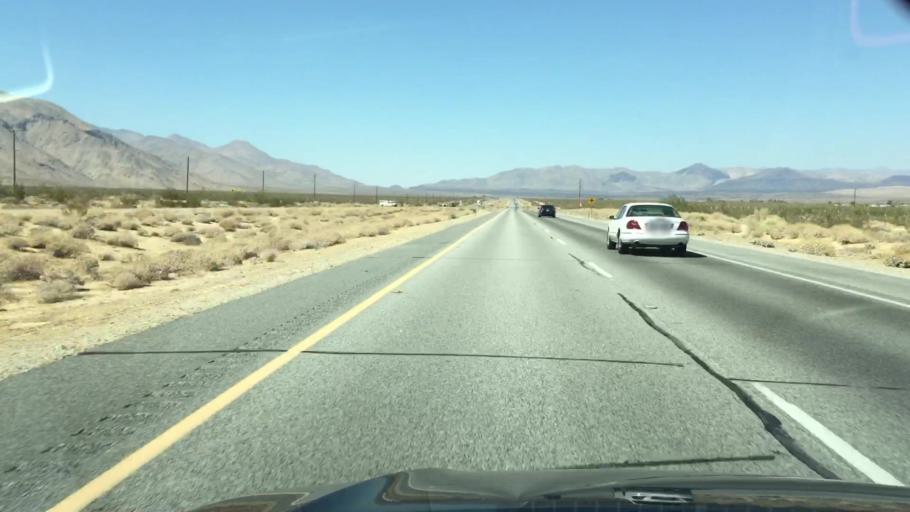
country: US
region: California
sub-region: Kern County
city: Inyokern
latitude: 35.7517
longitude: -117.8702
